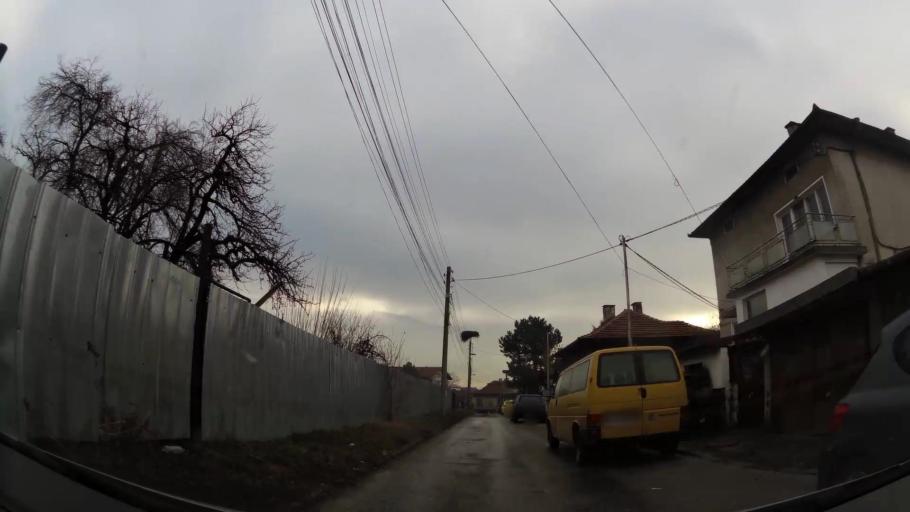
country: BG
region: Sofia-Capital
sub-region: Stolichna Obshtina
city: Sofia
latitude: 42.7464
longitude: 23.3477
